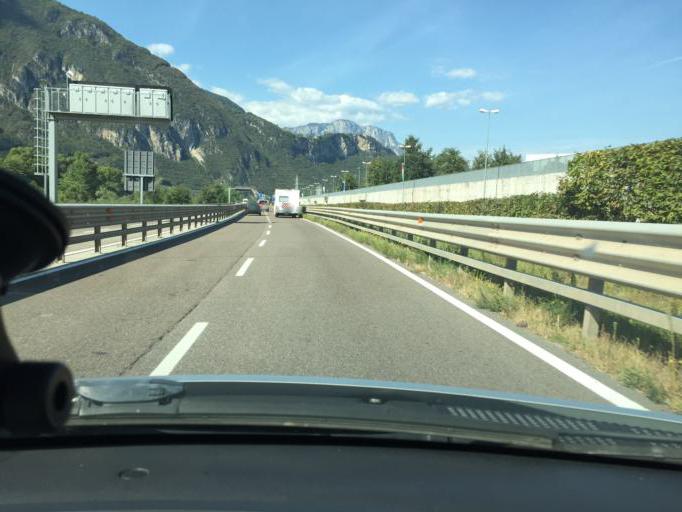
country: IT
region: Trentino-Alto Adige
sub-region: Provincia di Trento
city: Ravina
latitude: 46.0395
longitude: 11.1227
